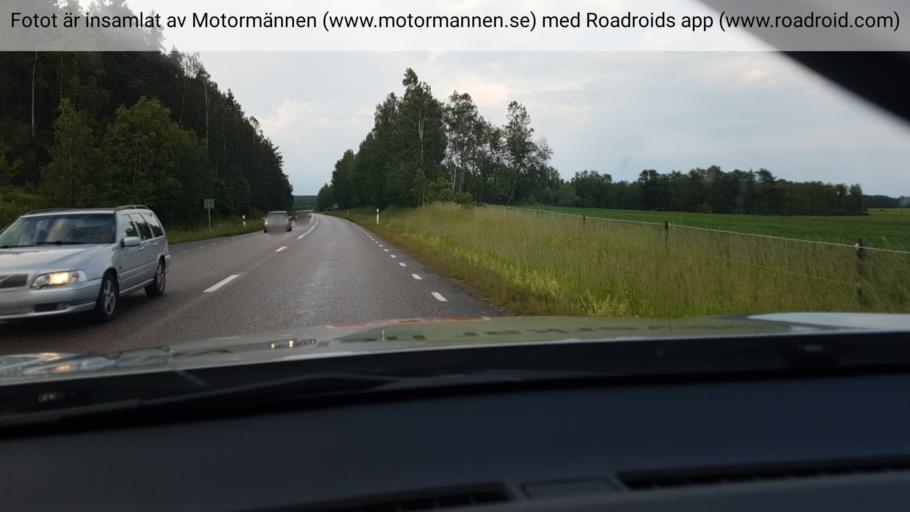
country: SE
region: Vaestra Goetaland
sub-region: Hjo Kommun
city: Hjo
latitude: 58.2420
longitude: 14.2280
